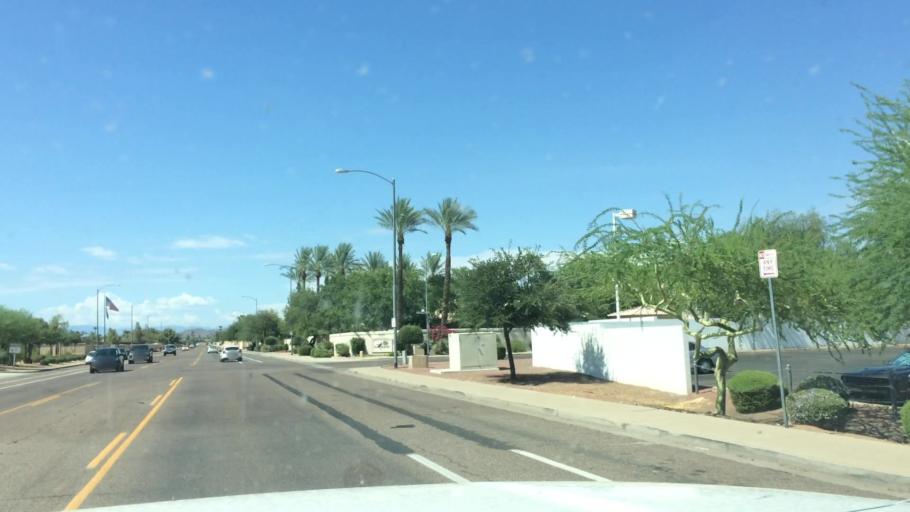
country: US
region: Arizona
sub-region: Maricopa County
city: Sun City
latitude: 33.6398
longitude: -112.2463
